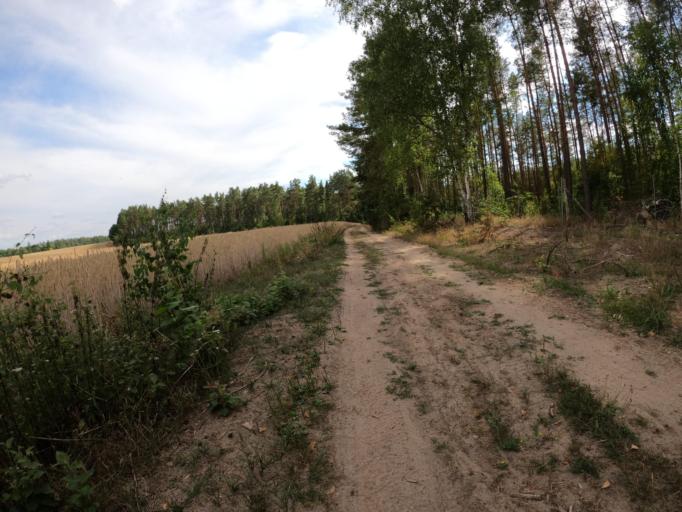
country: DE
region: Brandenburg
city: Lychen
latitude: 53.2708
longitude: 13.4380
